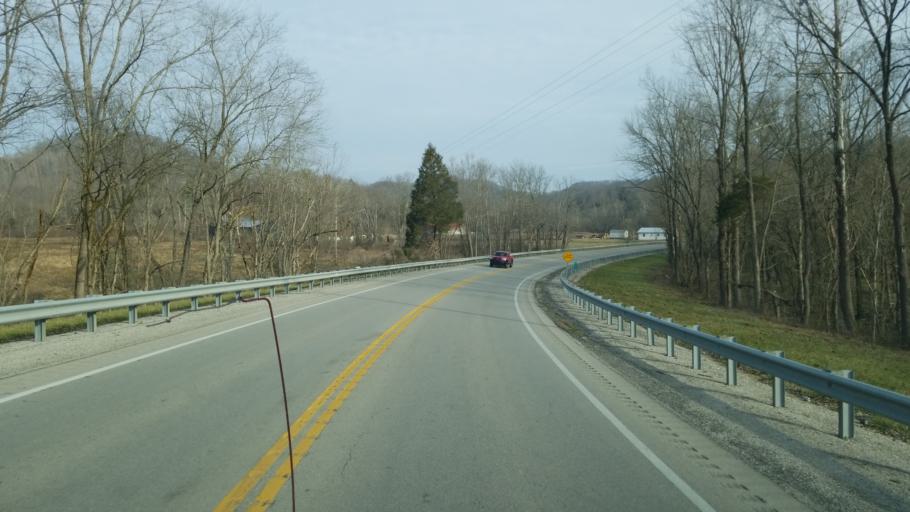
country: US
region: Kentucky
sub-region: Casey County
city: Liberty
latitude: 37.3358
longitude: -84.9085
